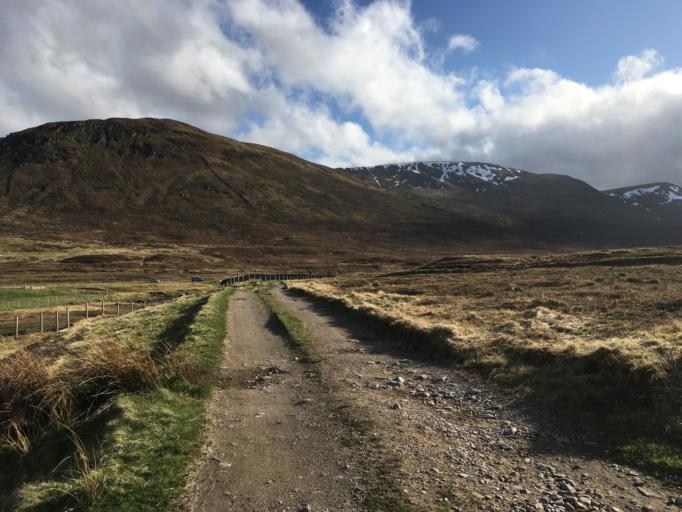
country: GB
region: Scotland
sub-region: Highland
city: Kingussie
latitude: 57.0223
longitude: -4.4353
